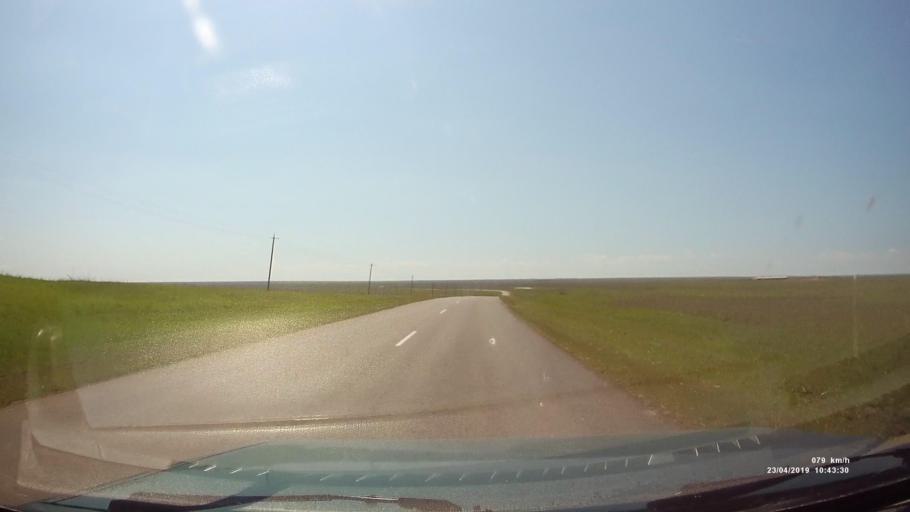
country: RU
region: Kalmykiya
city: Yashalta
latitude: 46.4694
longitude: 42.6500
